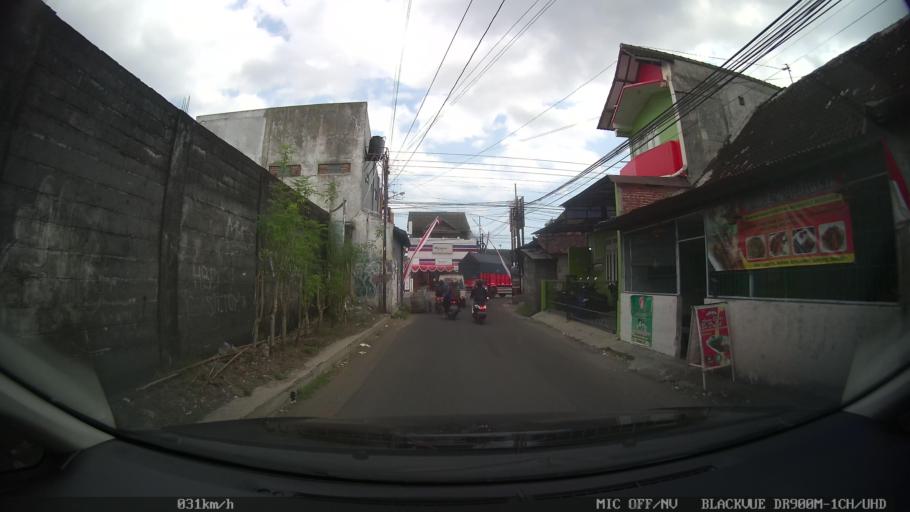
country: ID
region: Daerah Istimewa Yogyakarta
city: Gamping Lor
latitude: -7.7777
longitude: 110.3361
